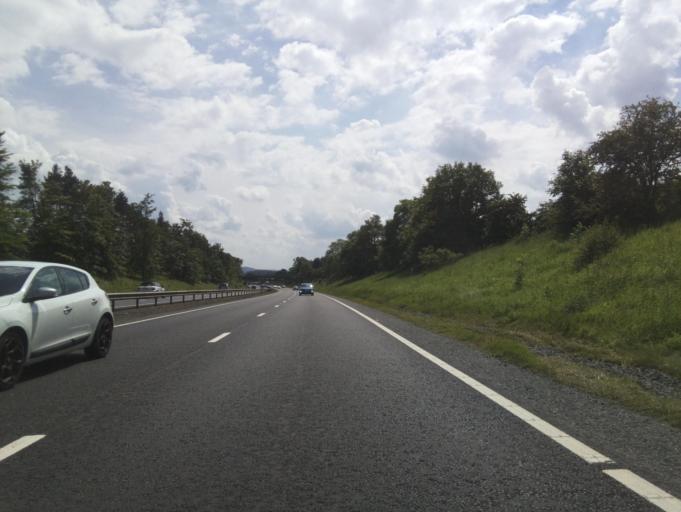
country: GB
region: England
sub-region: Stockton-on-Tees
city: Yarm
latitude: 54.4631
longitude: -1.3263
